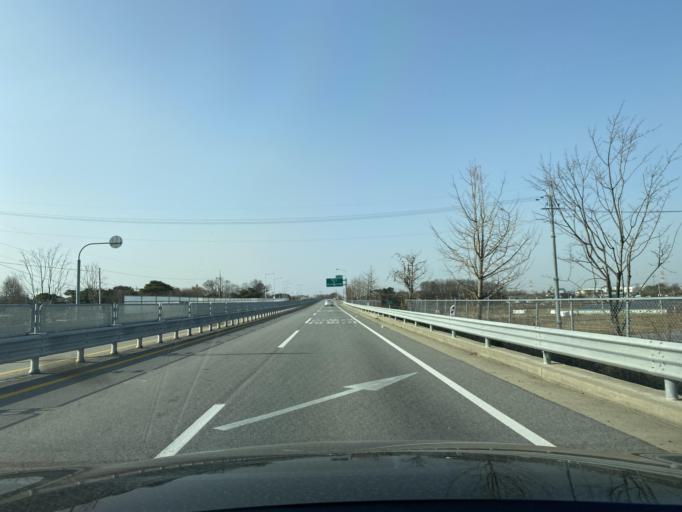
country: KR
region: Chungcheongnam-do
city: Yesan
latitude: 36.7578
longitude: 126.8260
